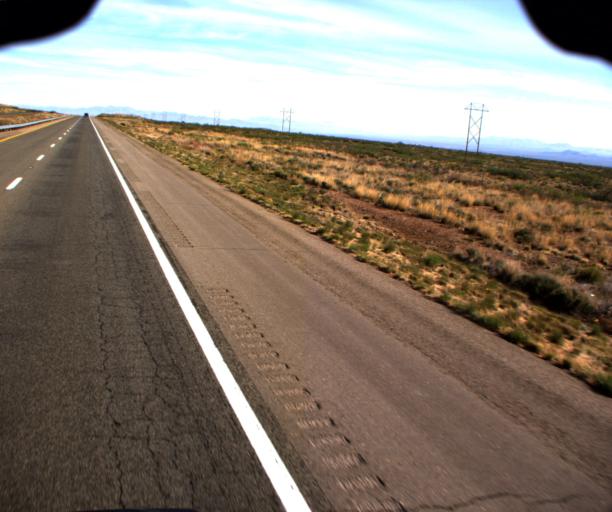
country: US
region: Arizona
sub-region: Graham County
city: Swift Trail Junction
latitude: 32.4959
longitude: -109.6735
